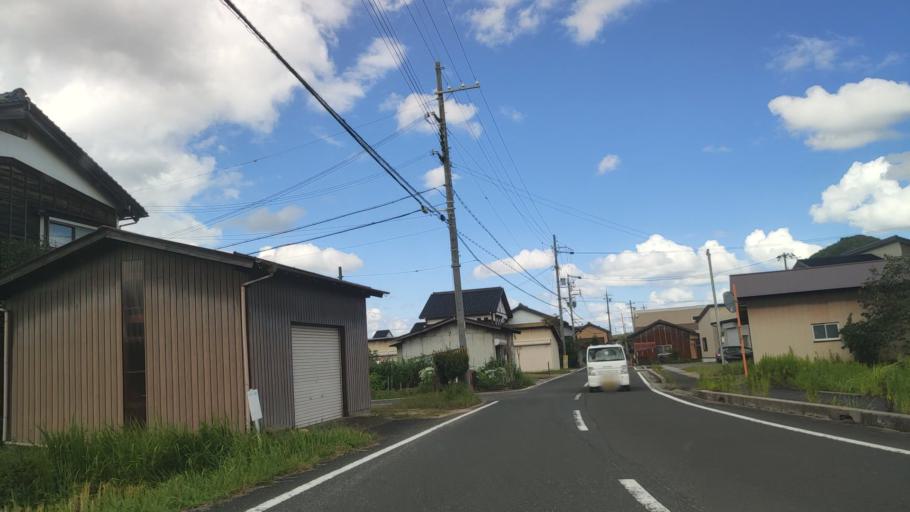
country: JP
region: Hyogo
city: Toyooka
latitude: 35.6036
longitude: 134.8978
